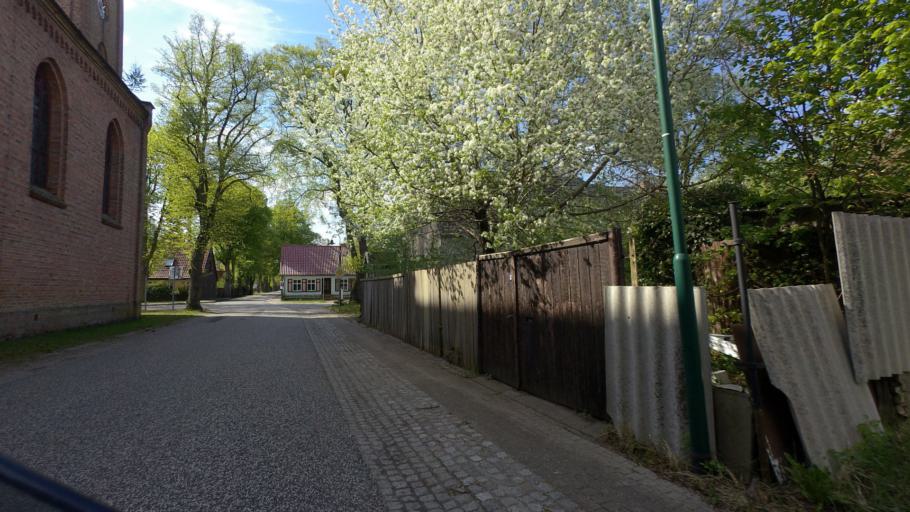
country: DE
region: Brandenburg
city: Templin
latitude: 52.9930
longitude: 13.5254
